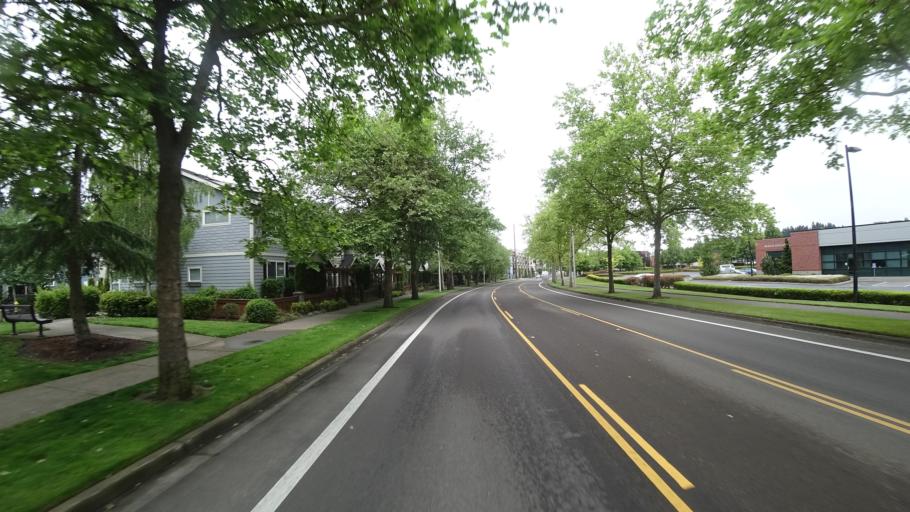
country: US
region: Oregon
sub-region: Washington County
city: Rockcreek
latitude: 45.5349
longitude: -122.8889
